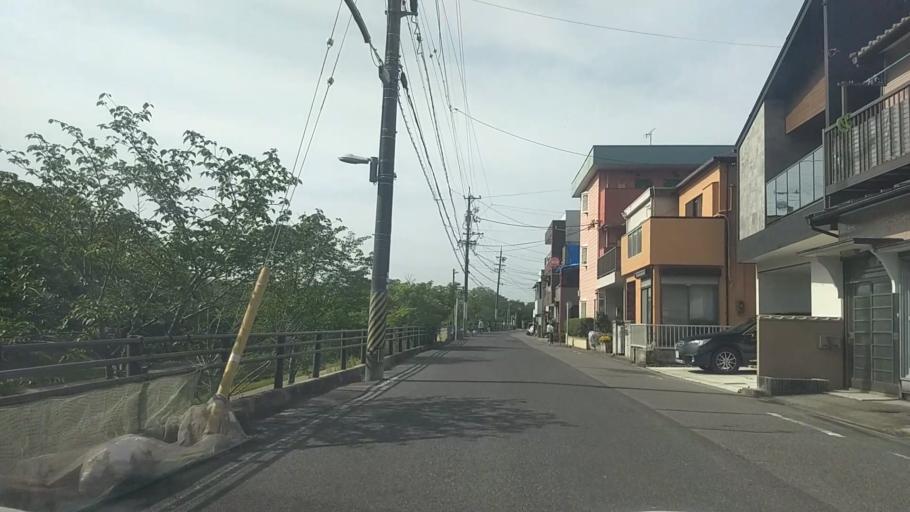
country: JP
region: Aichi
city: Okazaki
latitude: 34.9567
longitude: 137.1577
